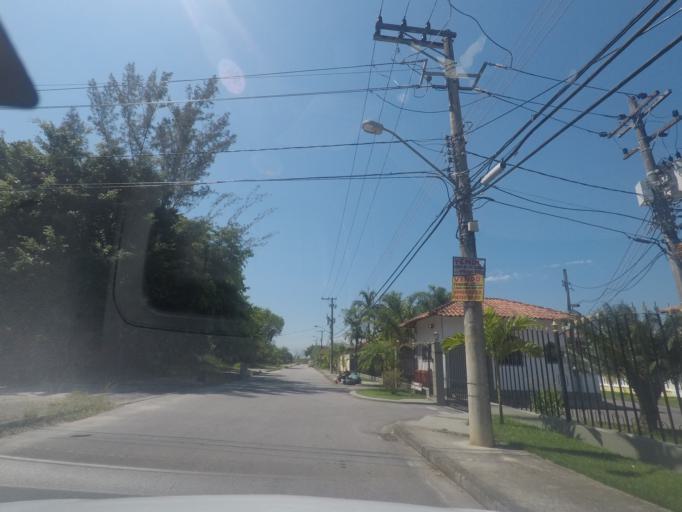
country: BR
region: Rio de Janeiro
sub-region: Nilopolis
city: Nilopolis
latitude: -22.9898
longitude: -43.4801
